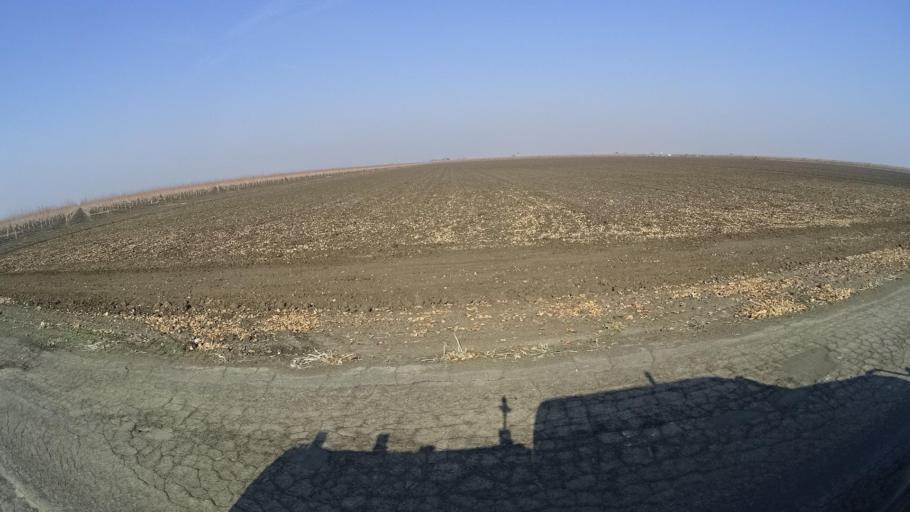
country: US
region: California
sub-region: Kern County
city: Buttonwillow
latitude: 35.3402
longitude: -119.4207
